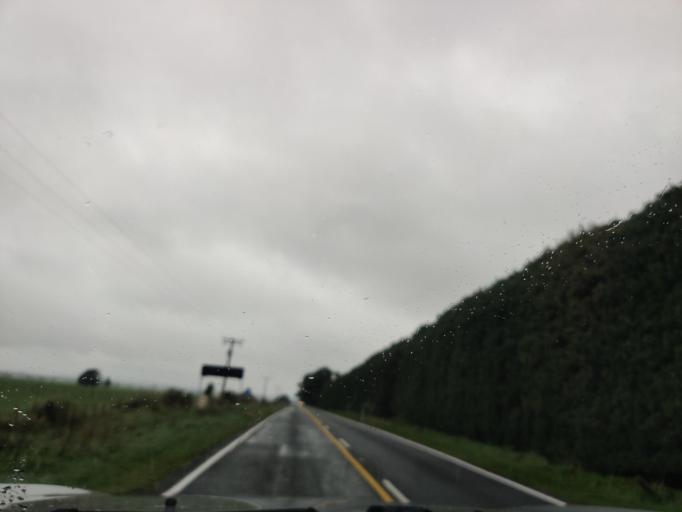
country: NZ
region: Manawatu-Wanganui
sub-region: Palmerston North City
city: Palmerston North
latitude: -40.0413
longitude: 176.2525
